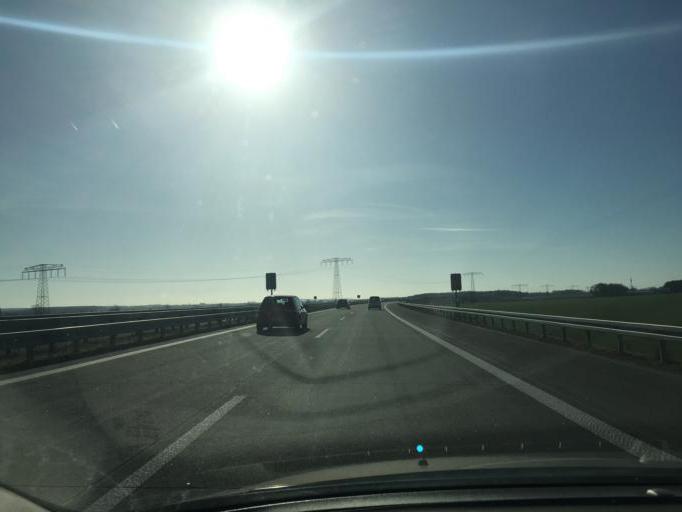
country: DE
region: Saxony
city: Frohburg
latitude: 51.0740
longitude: 12.6029
